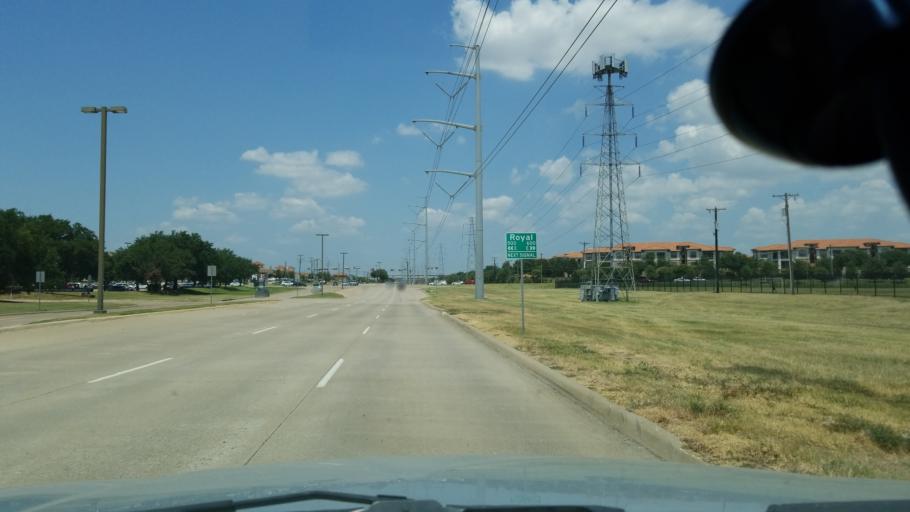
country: US
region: Texas
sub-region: Dallas County
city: Farmers Branch
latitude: 32.8937
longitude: -96.9373
